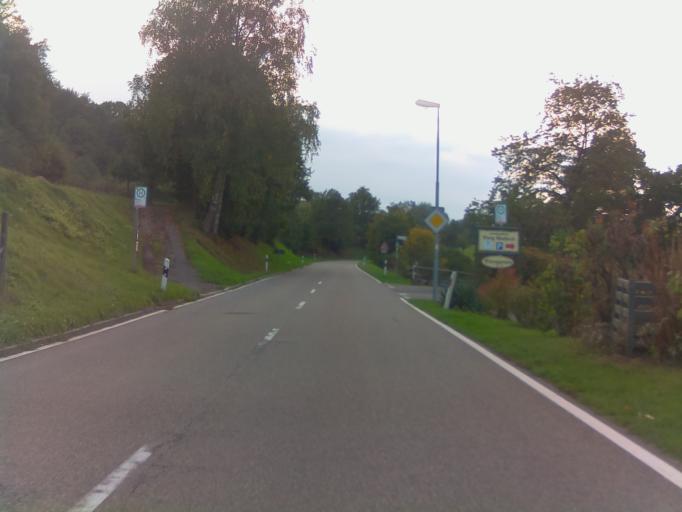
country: DE
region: Baden-Wuerttemberg
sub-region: Karlsruhe Region
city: Heiligkreuzsteinach
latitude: 49.4879
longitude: 8.7863
